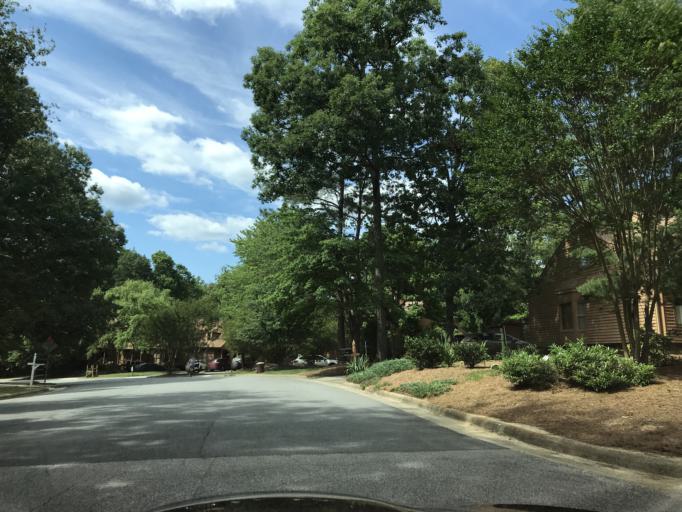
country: US
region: North Carolina
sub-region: Wake County
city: West Raleigh
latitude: 35.8822
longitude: -78.6842
